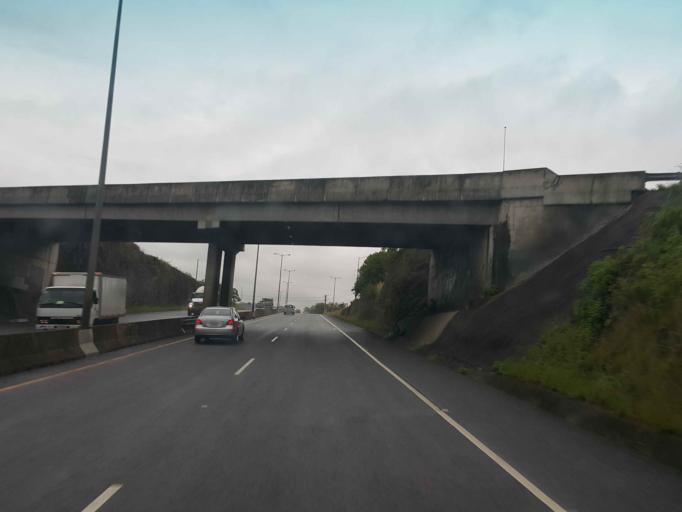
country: CR
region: Heredia
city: Colon
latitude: 9.9367
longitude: -84.2198
